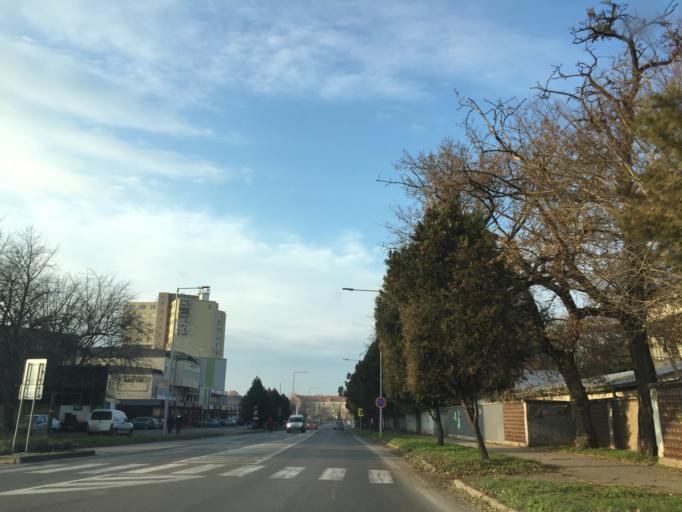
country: SK
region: Nitriansky
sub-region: Okres Nove Zamky
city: Nove Zamky
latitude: 47.9853
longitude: 18.1753
